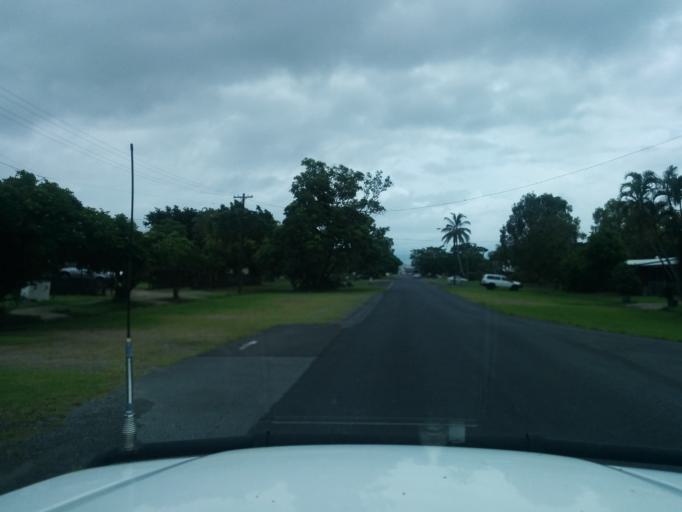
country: AU
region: Queensland
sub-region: Cairns
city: Cairns
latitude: -16.9317
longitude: 145.7549
